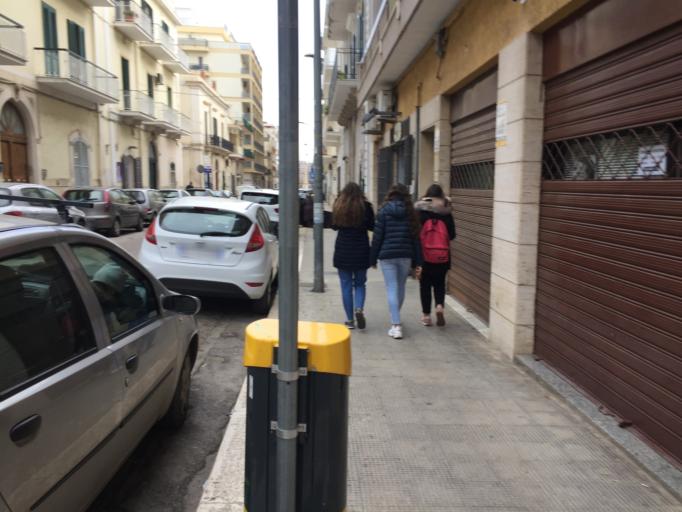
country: IT
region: Apulia
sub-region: Provincia di Bari
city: Bitonto
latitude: 41.1112
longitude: 16.6887
